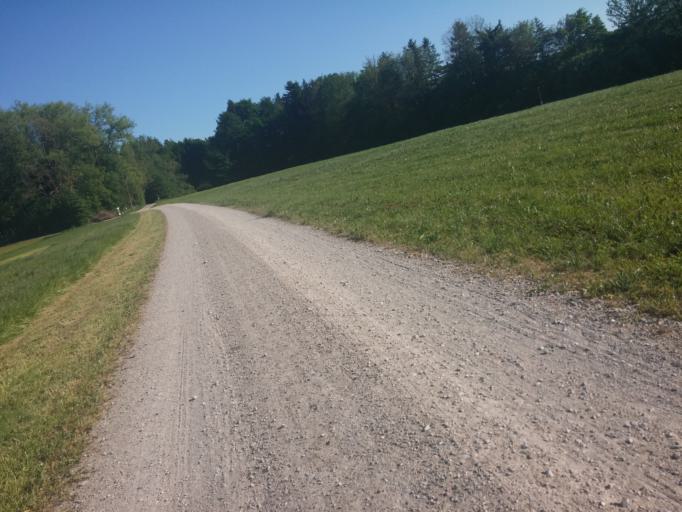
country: DE
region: Bavaria
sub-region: Swabia
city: Kronburg
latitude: 47.8755
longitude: 10.1770
